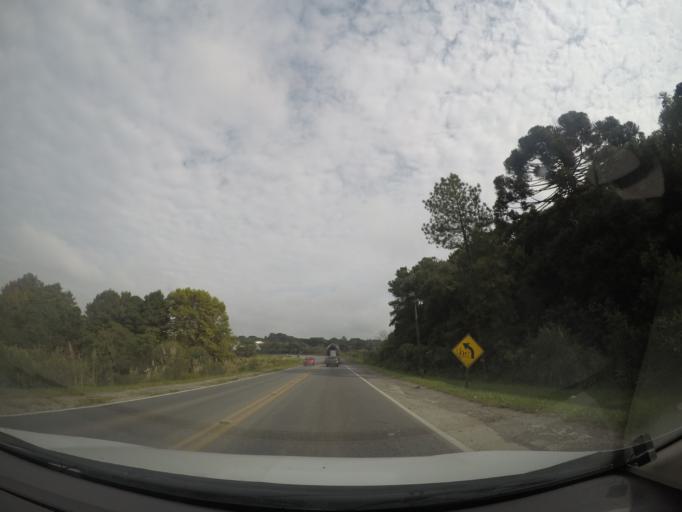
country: BR
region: Parana
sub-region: Colombo
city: Colombo
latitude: -25.3351
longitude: -49.2510
